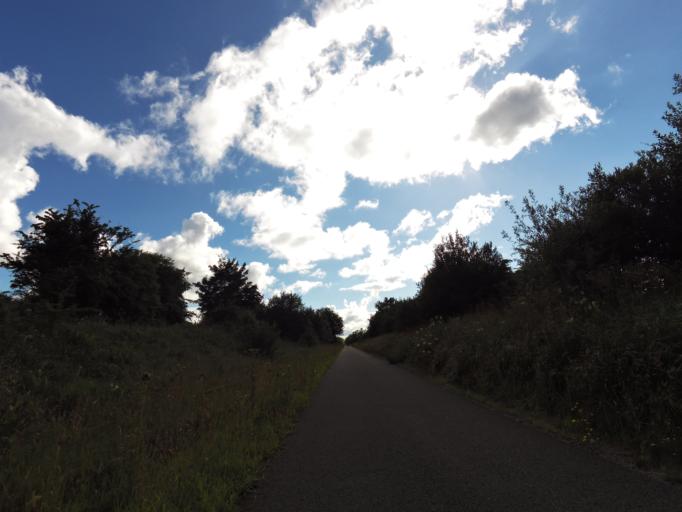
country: IE
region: Leinster
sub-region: An Iarmhi
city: Kilbeggan
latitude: 53.4440
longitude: -7.5455
